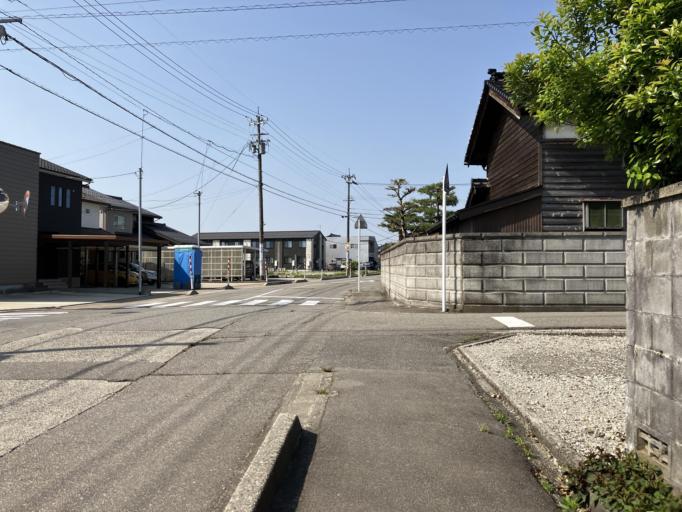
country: JP
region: Toyama
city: Takaoka
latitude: 36.7465
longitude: 137.0258
